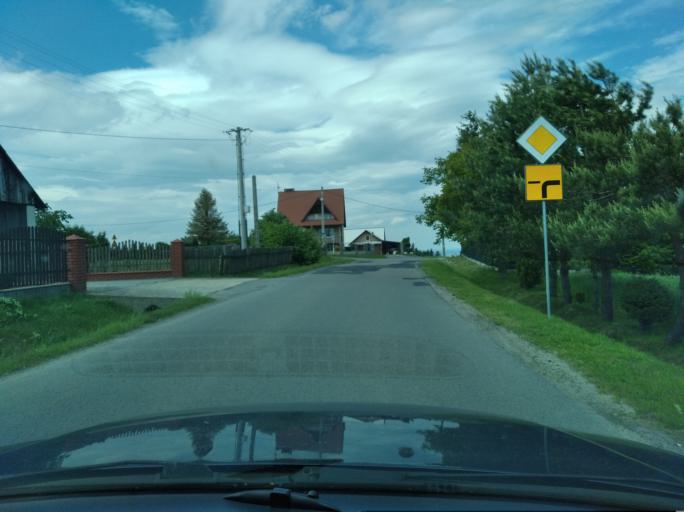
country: PL
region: Subcarpathian Voivodeship
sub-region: Powiat ropczycko-sedziszowski
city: Ropczyce
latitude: 50.0240
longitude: 21.6044
